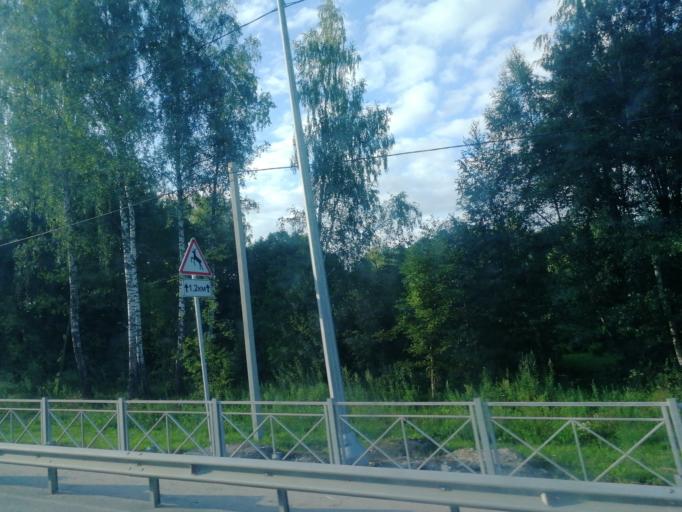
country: RU
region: Kaluga
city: Kaluga
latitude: 54.4373
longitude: 36.3409
